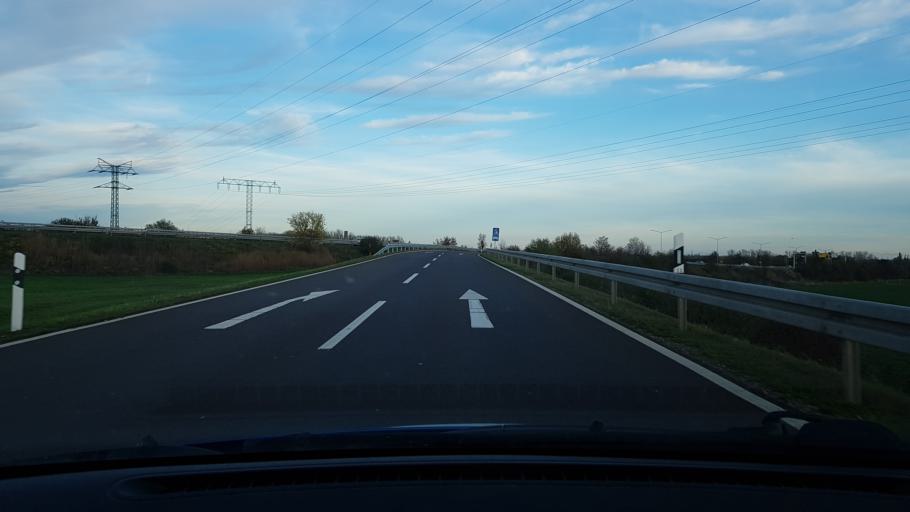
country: DE
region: Saxony-Anhalt
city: Barleben
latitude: 52.1846
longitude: 11.6184
